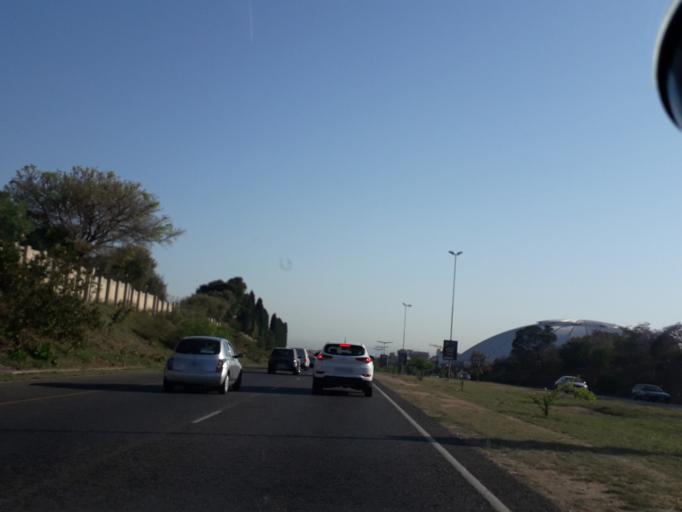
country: ZA
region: Gauteng
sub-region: West Rand District Municipality
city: Muldersdriseloop
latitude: -26.0667
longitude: 27.9397
